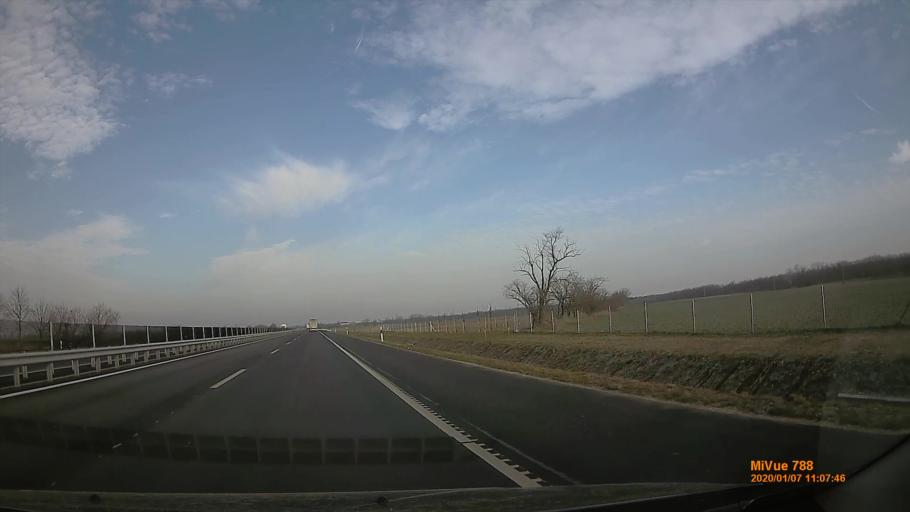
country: HU
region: Gyor-Moson-Sopron
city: Rajka
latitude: 47.9763
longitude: 17.1800
